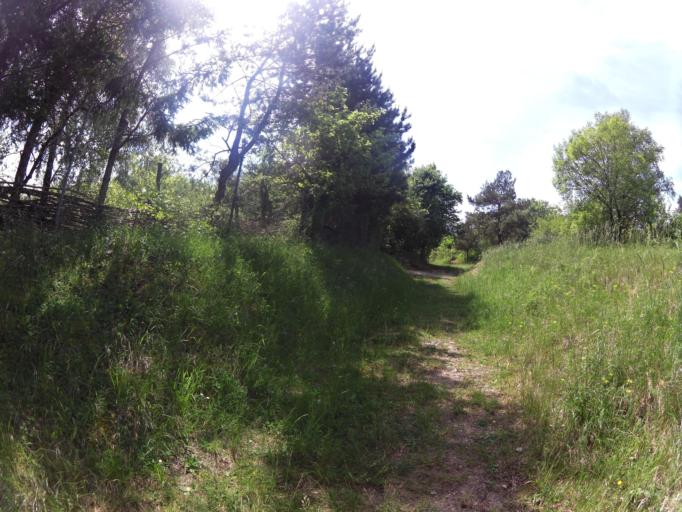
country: DE
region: Bavaria
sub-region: Regierungsbezirk Unterfranken
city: Sommerhausen
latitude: 49.6757
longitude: 10.0278
